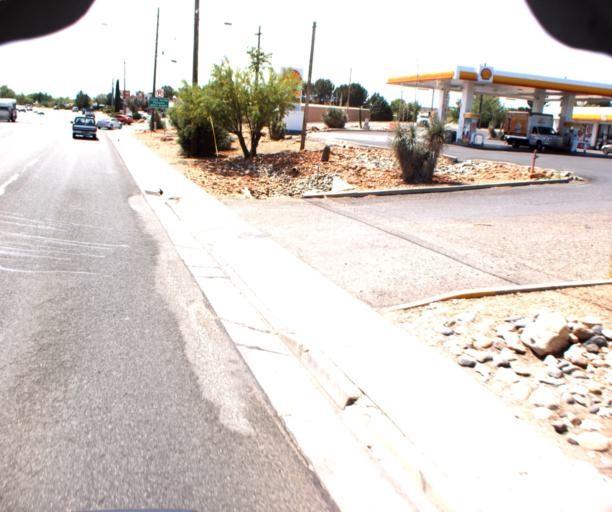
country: US
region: Arizona
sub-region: Yavapai County
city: Verde Village
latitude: 34.7239
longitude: -112.0060
